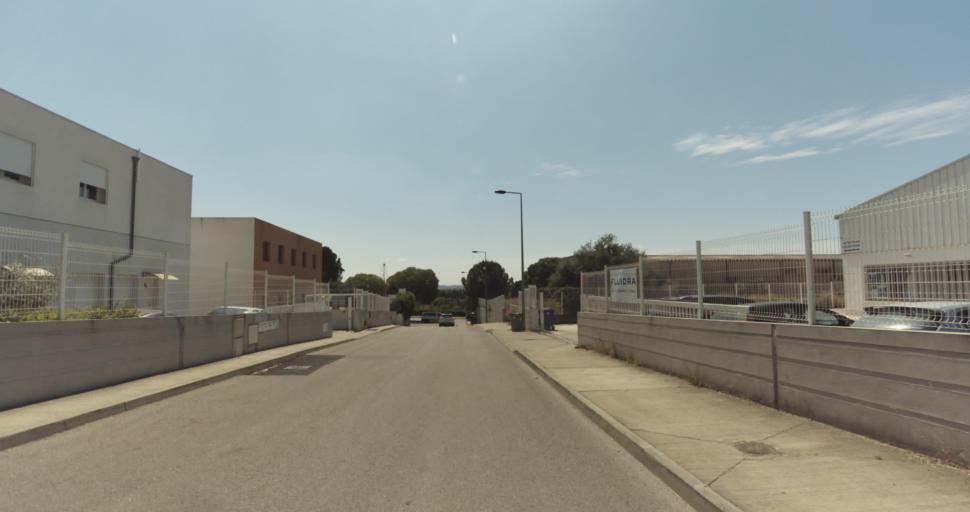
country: FR
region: Languedoc-Roussillon
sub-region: Departement du Gard
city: Milhaud
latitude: 43.8163
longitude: 4.3132
